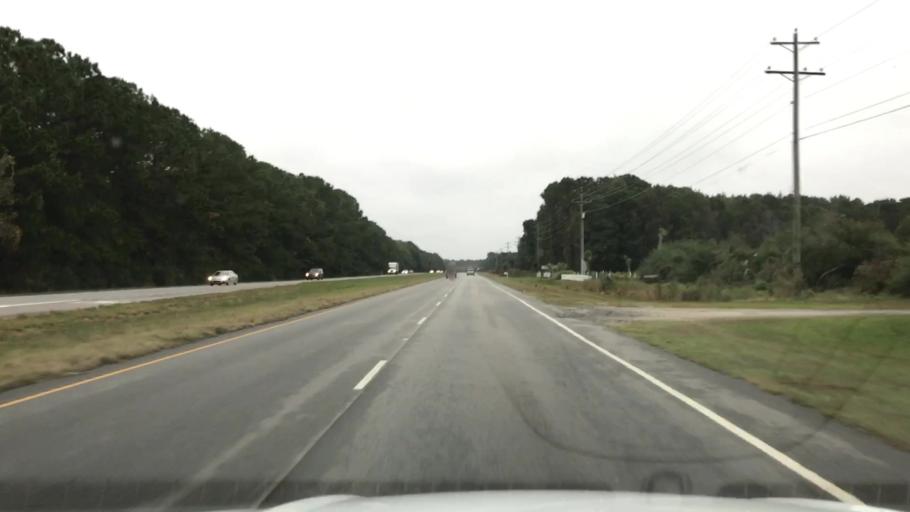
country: US
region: South Carolina
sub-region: Charleston County
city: Isle of Palms
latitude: 32.9099
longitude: -79.7233
